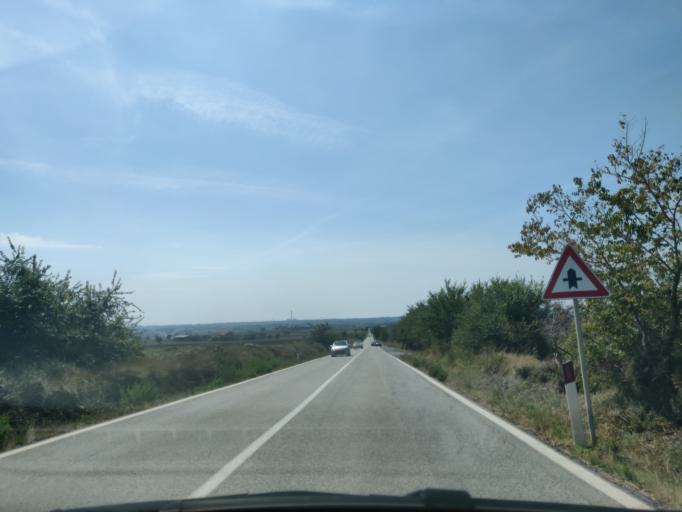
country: IT
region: Latium
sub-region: Provincia di Viterbo
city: Tarquinia
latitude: 42.2218
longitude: 11.7861
